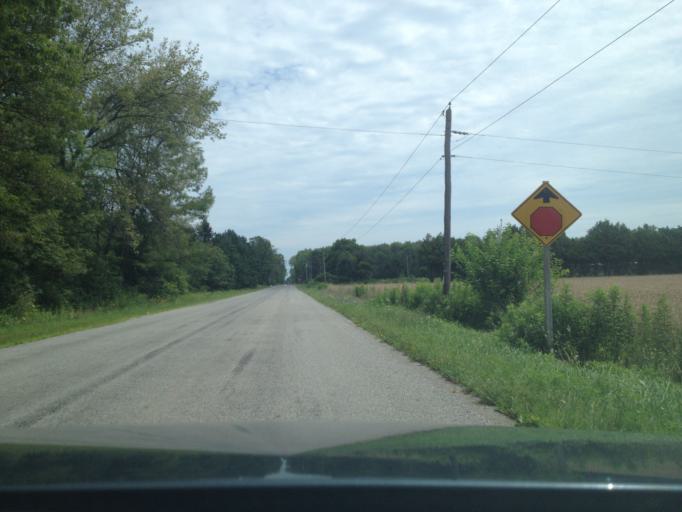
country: CA
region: Ontario
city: Norfolk County
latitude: 42.8543
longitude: -80.4057
